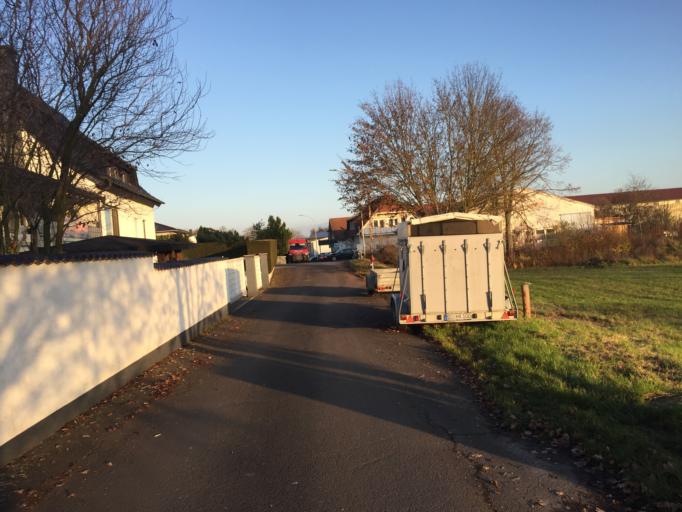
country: DE
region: Hesse
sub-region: Regierungsbezirk Darmstadt
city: Munzenberg
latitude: 50.4779
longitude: 8.7601
